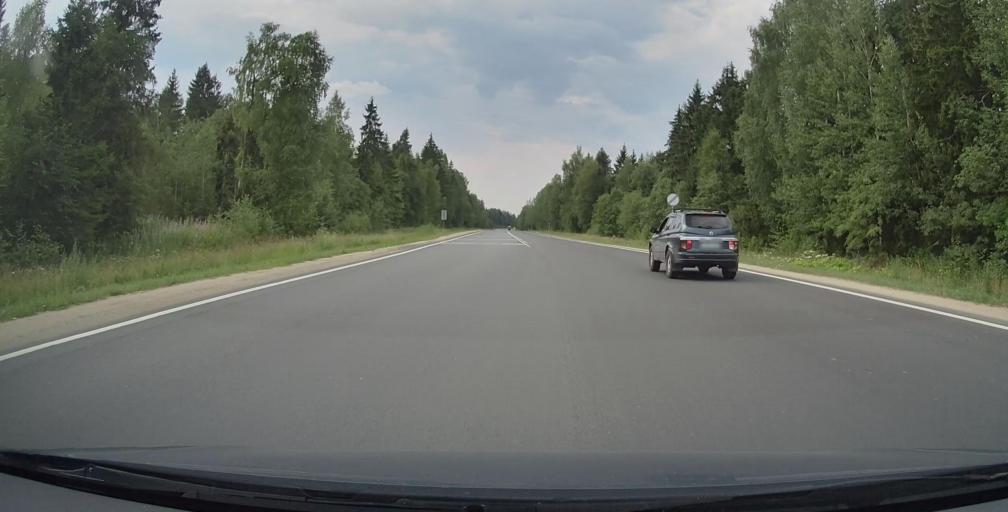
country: RU
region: Jaroslavl
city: Tutayev
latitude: 57.8940
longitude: 39.4206
